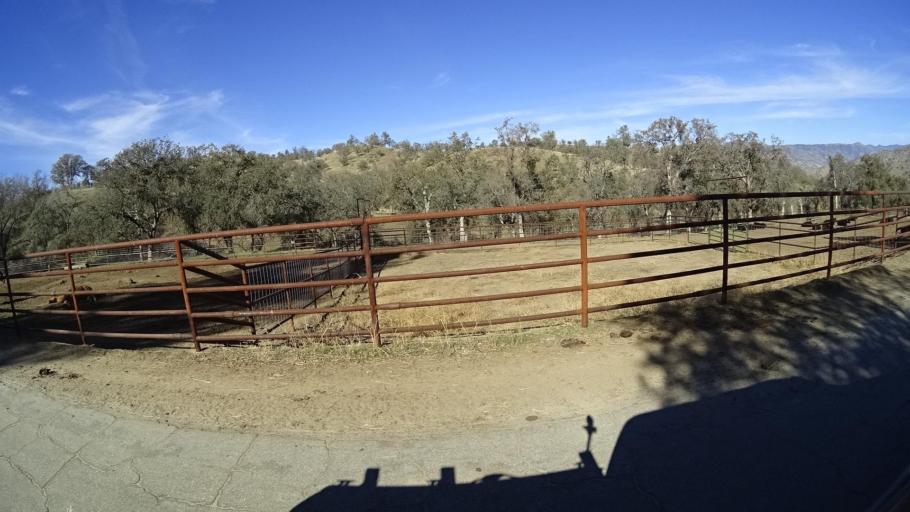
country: US
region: California
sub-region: Kern County
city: Arvin
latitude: 35.4419
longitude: -118.7169
